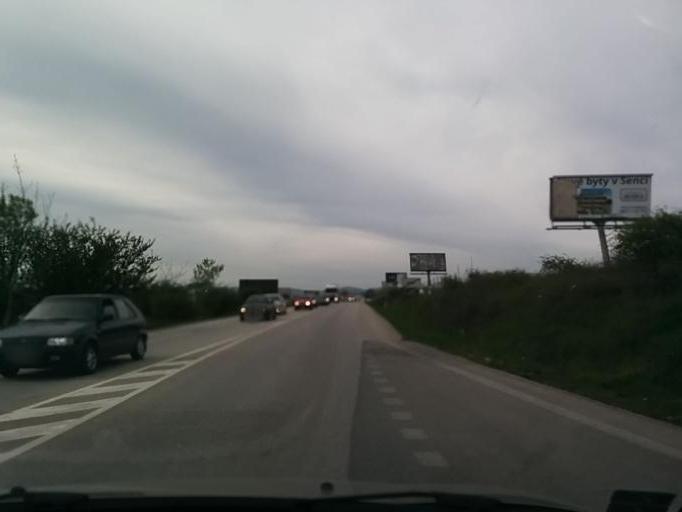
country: SK
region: Bratislavsky
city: Senec
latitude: 48.2245
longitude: 17.3830
